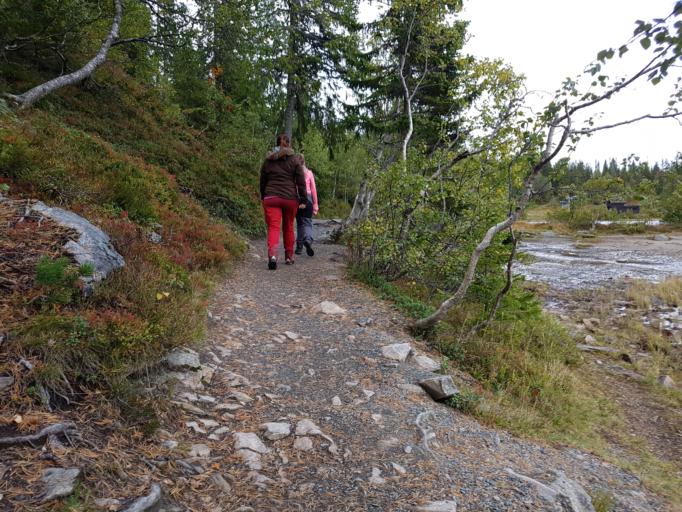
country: NO
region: Sor-Trondelag
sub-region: Melhus
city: Melhus
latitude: 63.4153
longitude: 10.2517
